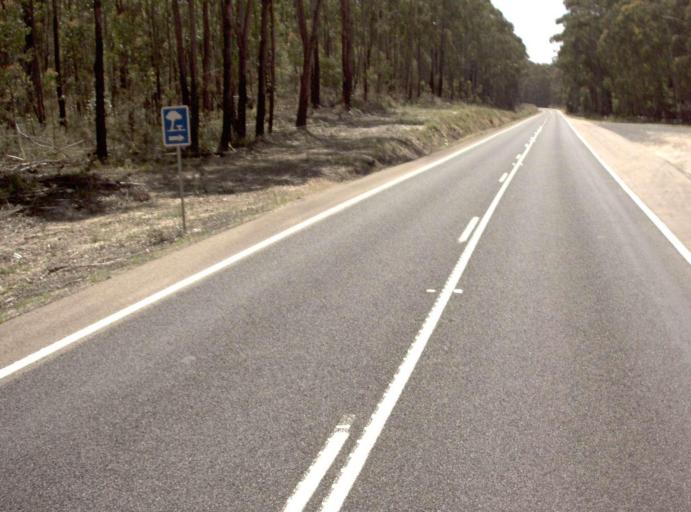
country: AU
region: New South Wales
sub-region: Bombala
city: Bombala
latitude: -37.5757
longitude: 149.3069
